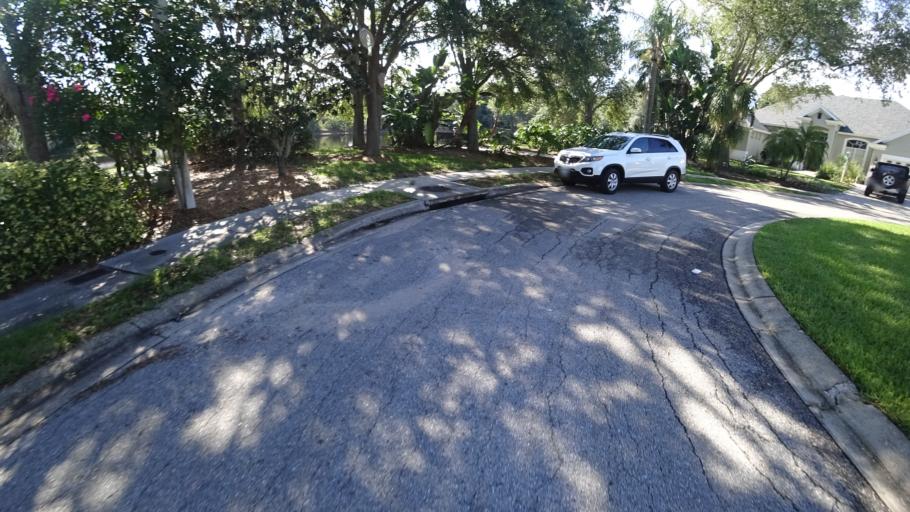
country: US
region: Florida
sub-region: Manatee County
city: West Bradenton
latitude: 27.5101
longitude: -82.6477
